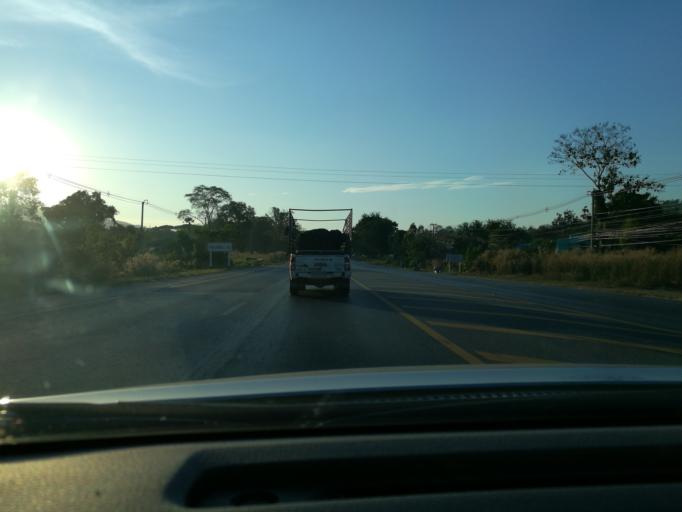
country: TH
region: Phitsanulok
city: Wang Thong
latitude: 16.8429
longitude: 100.5442
